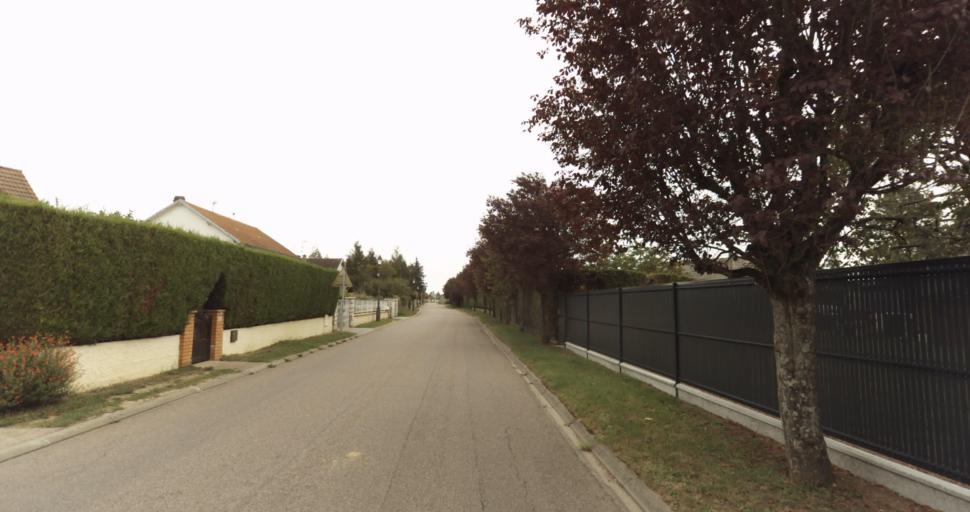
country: FR
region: Haute-Normandie
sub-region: Departement de l'Eure
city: Marcilly-sur-Eure
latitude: 48.8625
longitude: 1.3391
